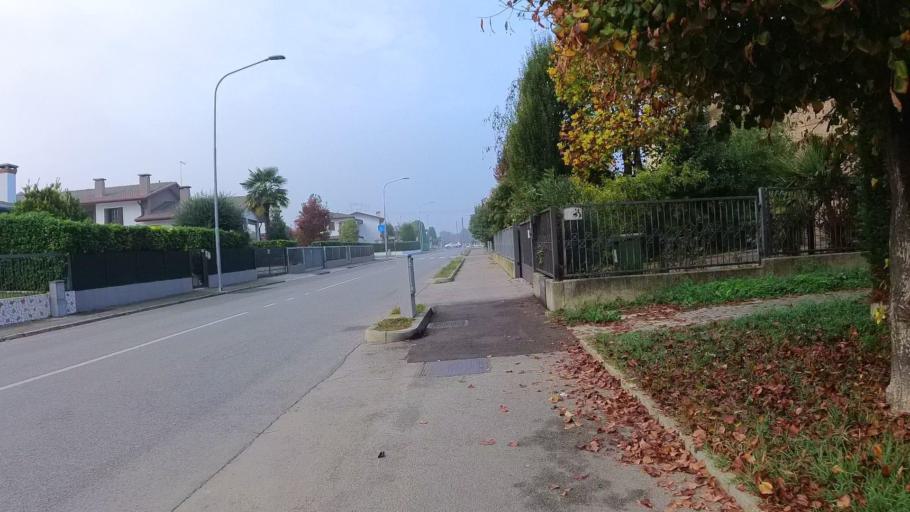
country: IT
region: Veneto
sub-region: Provincia di Venezia
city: Fosso
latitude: 45.3661
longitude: 12.0447
